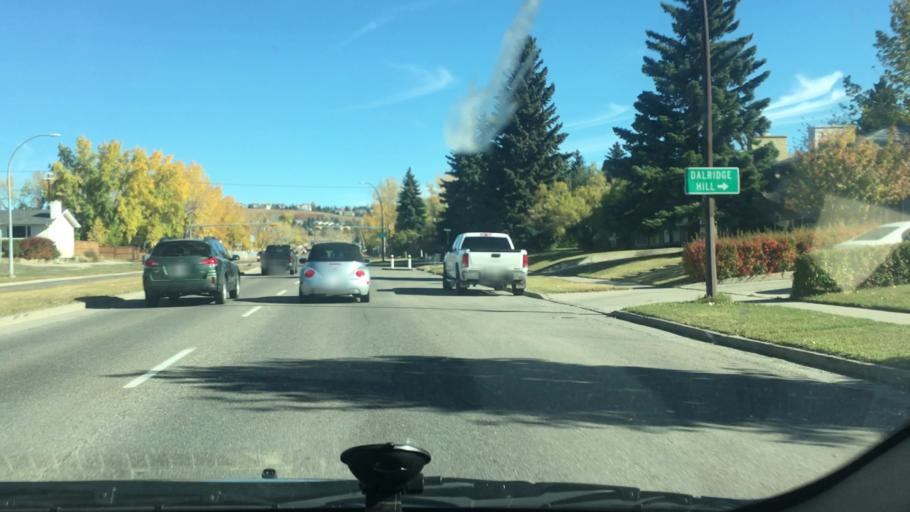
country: CA
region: Alberta
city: Calgary
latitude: 51.1098
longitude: -114.1600
